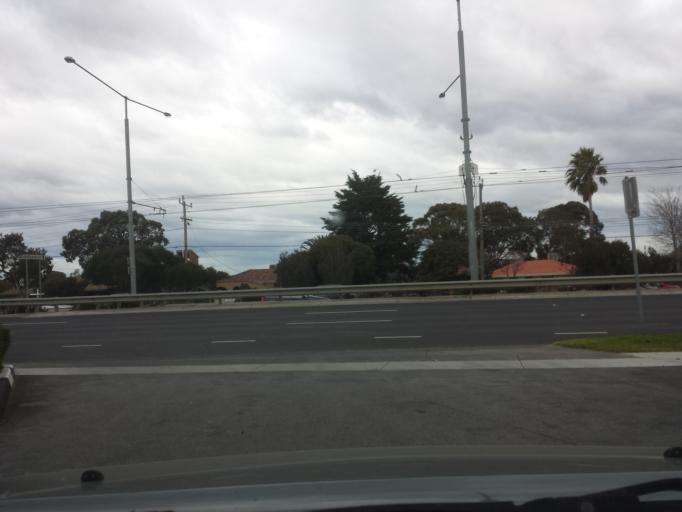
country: AU
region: Victoria
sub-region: Whitehorse
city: Vermont South
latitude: -37.8558
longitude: 145.1814
